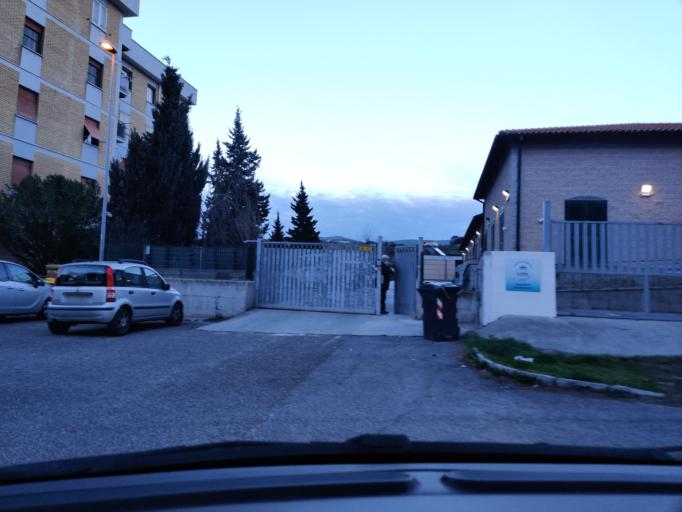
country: IT
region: Latium
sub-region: Citta metropolitana di Roma Capitale
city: Civitavecchia
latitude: 42.0786
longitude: 11.8163
